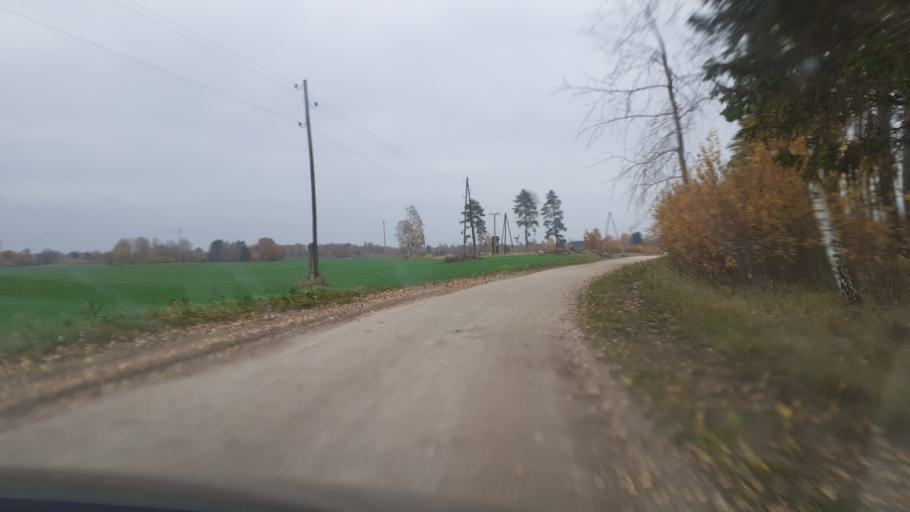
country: LV
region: Saldus Rajons
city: Saldus
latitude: 56.8667
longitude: 22.3108
